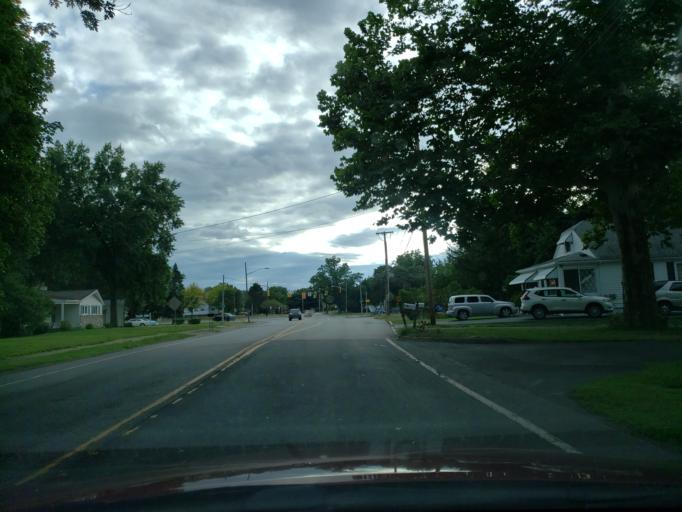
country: US
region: New York
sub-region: Monroe County
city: Greece
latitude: 43.2162
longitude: -77.6578
